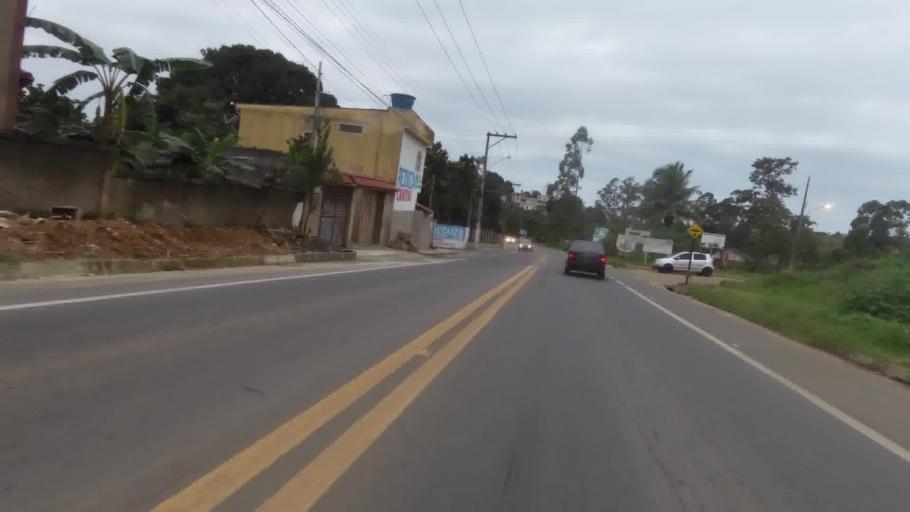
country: BR
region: Espirito Santo
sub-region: Piuma
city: Piuma
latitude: -20.8320
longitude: -40.7081
